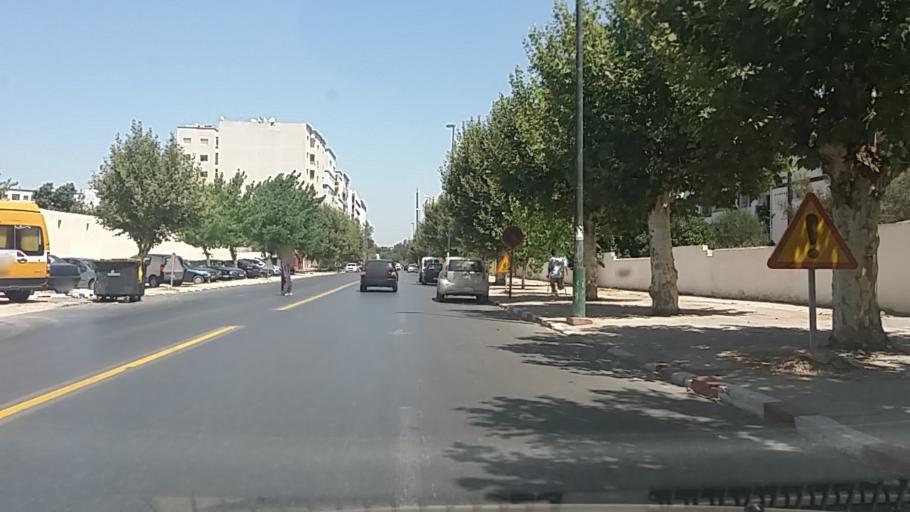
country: MA
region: Gharb-Chrarda-Beni Hssen
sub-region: Kenitra Province
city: Kenitra
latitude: 34.2543
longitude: -6.5787
